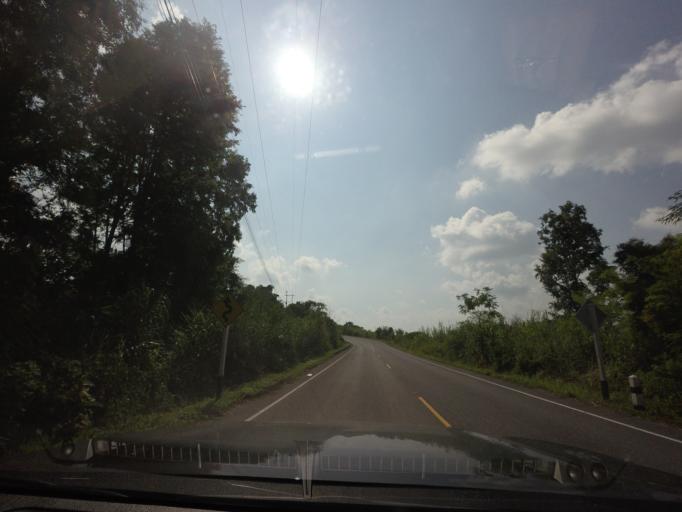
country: TH
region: Nan
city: Santi Suk
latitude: 18.9735
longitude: 101.0285
